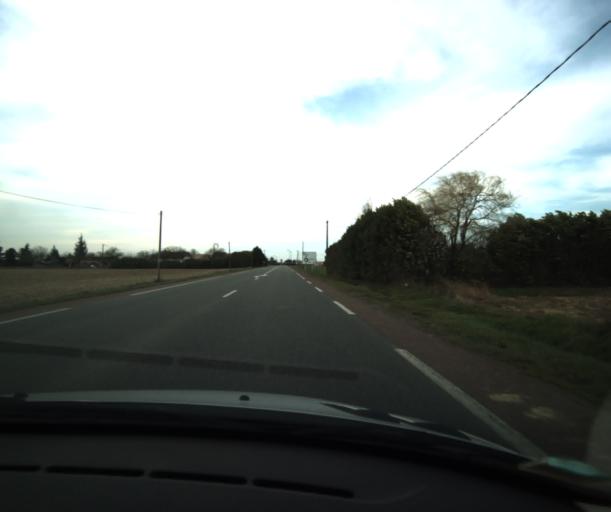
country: FR
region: Midi-Pyrenees
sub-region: Departement du Tarn-et-Garonne
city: Montech
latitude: 43.9733
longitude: 1.2031
